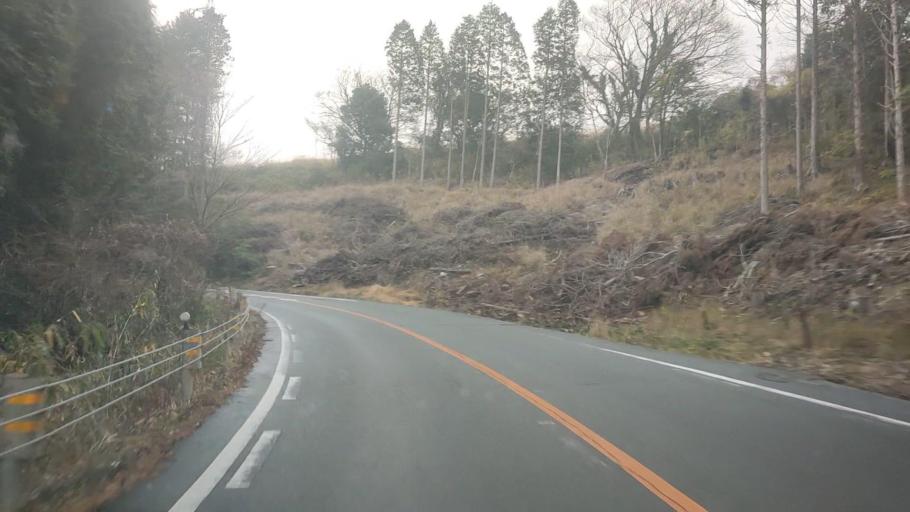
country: JP
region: Kumamoto
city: Aso
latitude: 32.8973
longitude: 130.9986
